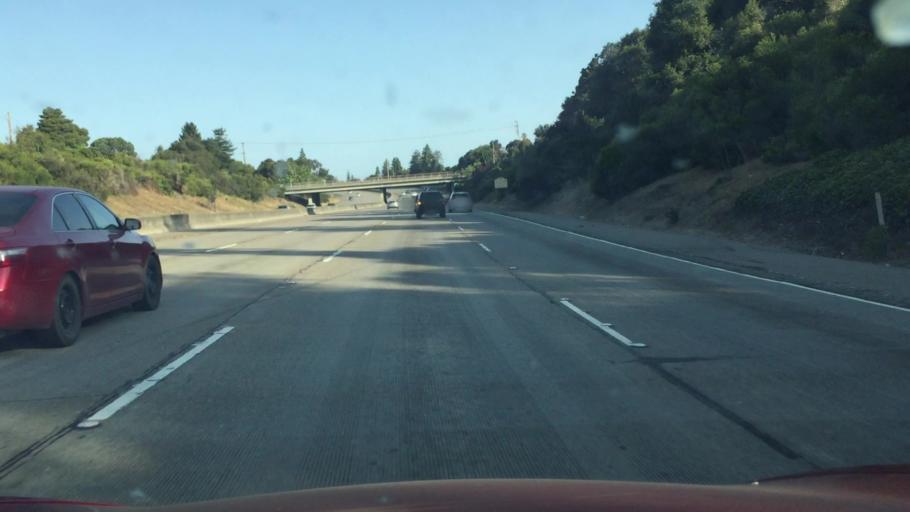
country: US
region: California
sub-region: Alameda County
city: Piedmont
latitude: 37.7901
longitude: -122.2013
